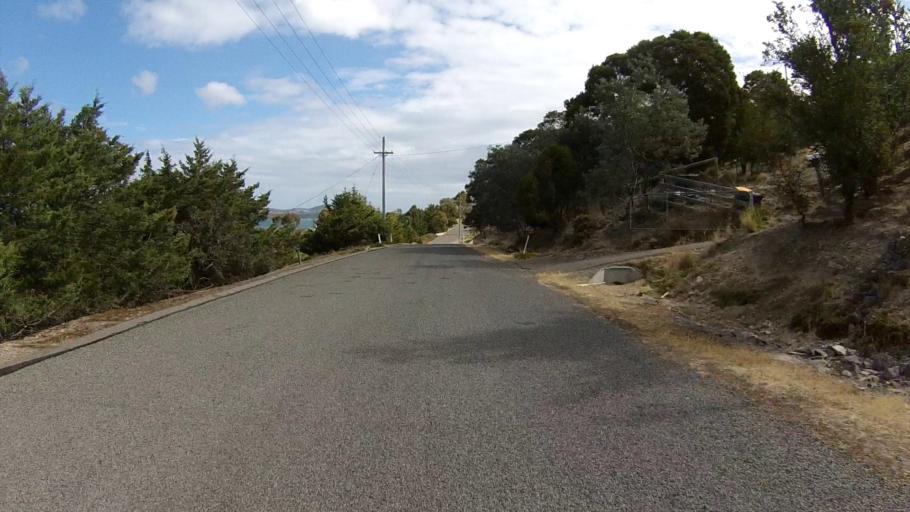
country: AU
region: Tasmania
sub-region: Clarence
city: Acton Park
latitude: -42.8814
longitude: 147.5042
